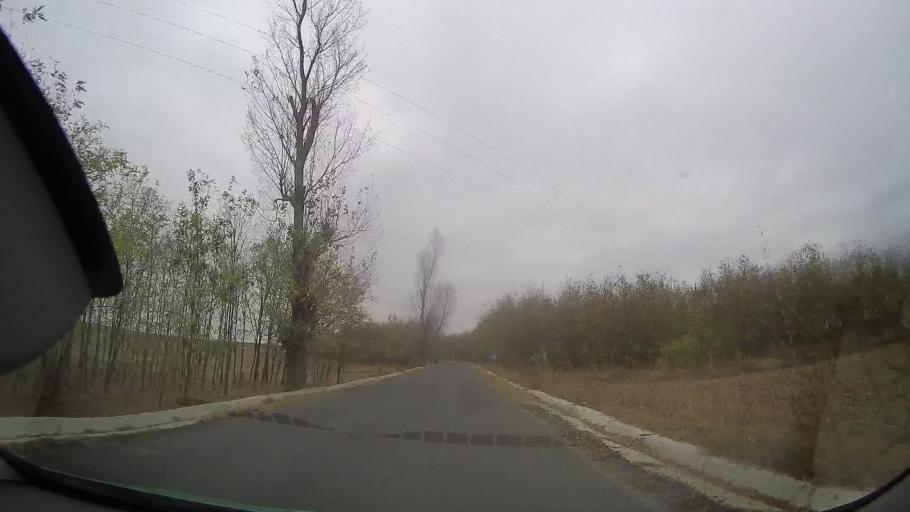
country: RO
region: Braila
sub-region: Comuna Ciocile
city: Ciocile
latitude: 44.7961
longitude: 27.2755
